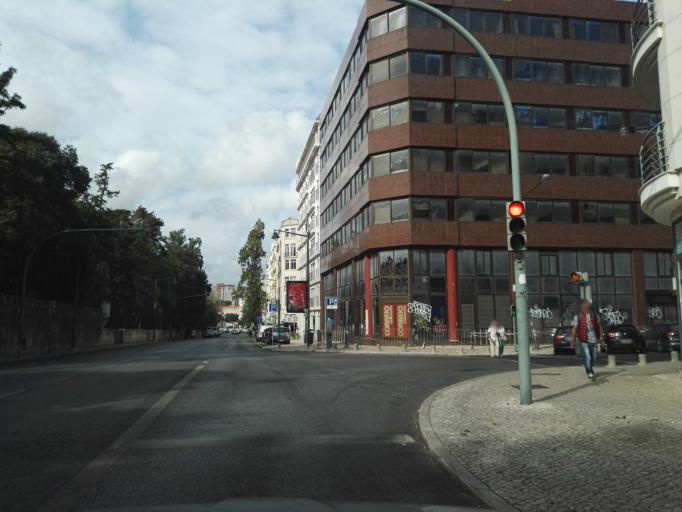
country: PT
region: Lisbon
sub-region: Lisbon
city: Lisbon
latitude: 38.7354
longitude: -9.1521
